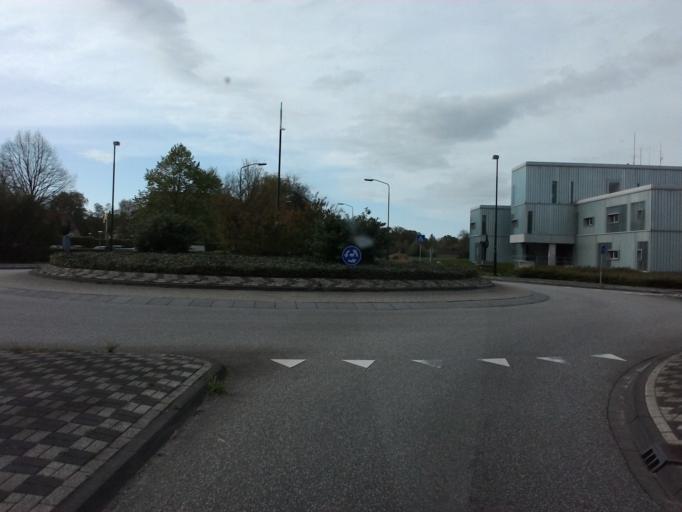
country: NL
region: North Brabant
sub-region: Gemeente Boxtel
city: Boxtel
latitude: 51.6018
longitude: 5.3223
